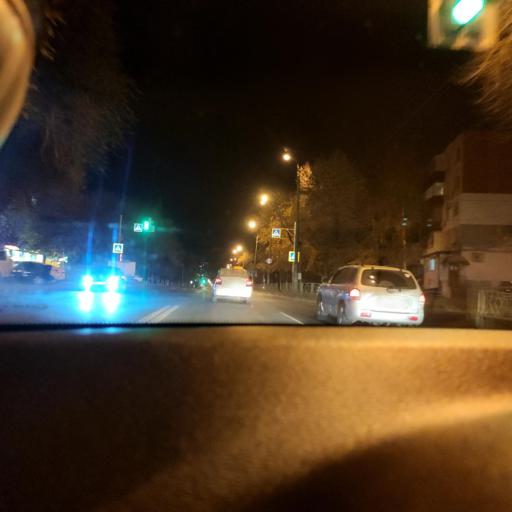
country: RU
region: Samara
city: Samara
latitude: 53.2530
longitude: 50.2352
